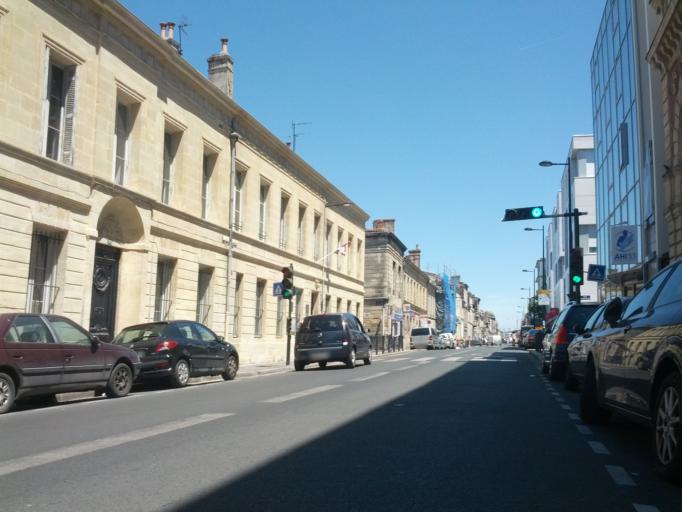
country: FR
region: Aquitaine
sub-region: Departement de la Gironde
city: Bordeaux
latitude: 44.8562
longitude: -0.5699
